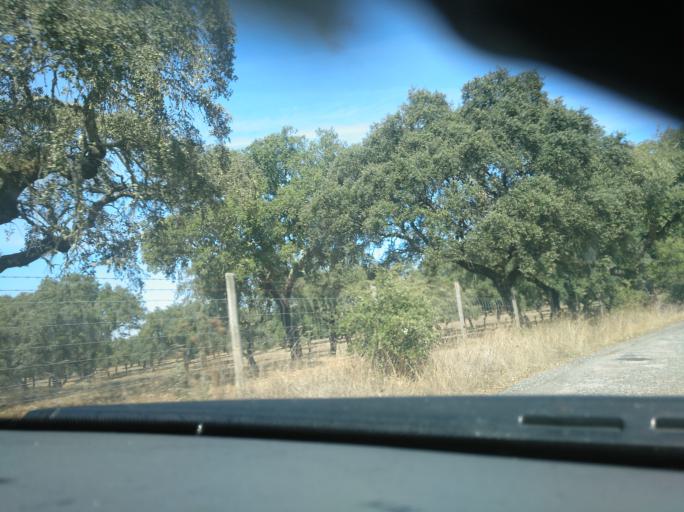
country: PT
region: Evora
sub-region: Arraiolos
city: Arraiolos
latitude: 38.6922
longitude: -8.0943
